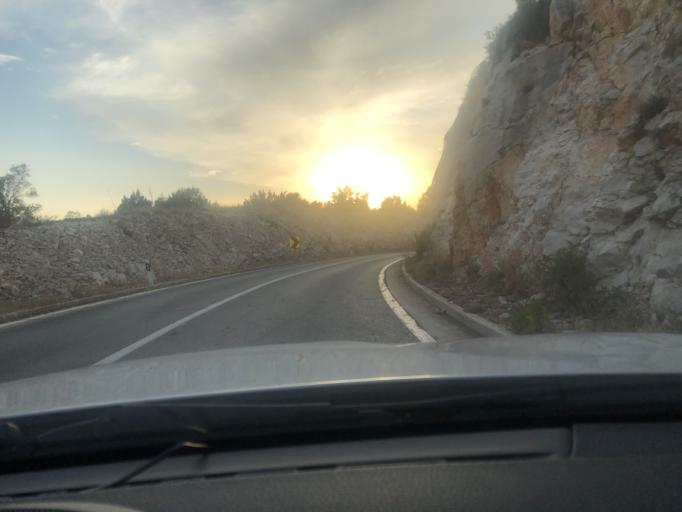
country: HR
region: Splitsko-Dalmatinska
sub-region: Grad Hvar
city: Hvar
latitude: 43.1600
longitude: 16.4983
